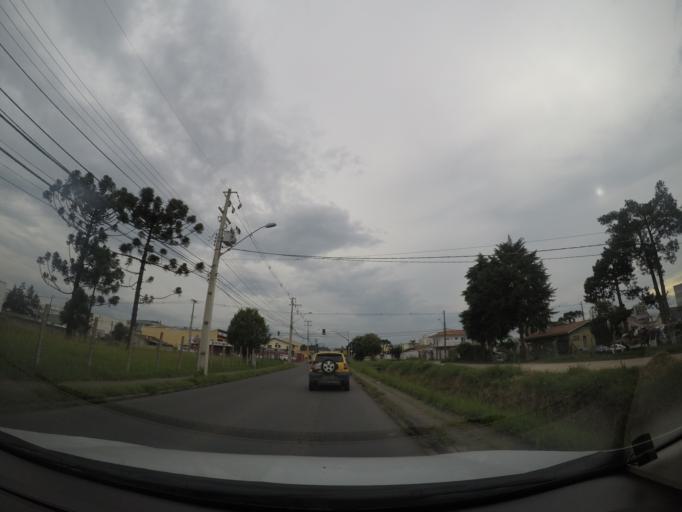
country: BR
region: Parana
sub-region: Sao Jose Dos Pinhais
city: Sao Jose dos Pinhais
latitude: -25.4942
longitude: -49.2364
